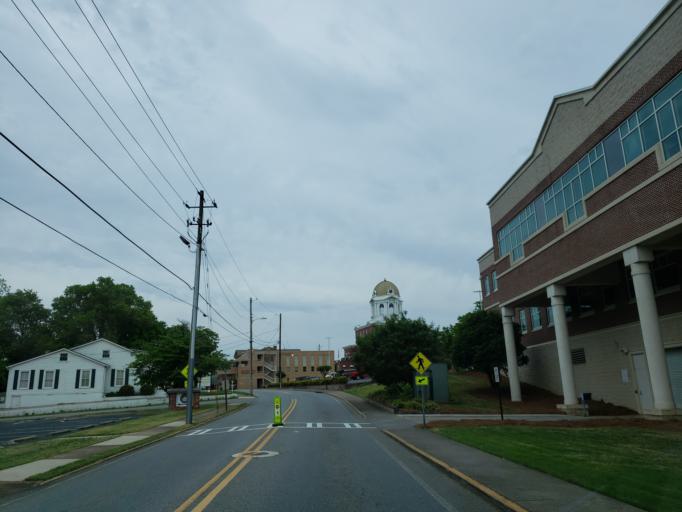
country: US
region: Georgia
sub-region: Bartow County
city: Cartersville
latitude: 34.1661
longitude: -84.7999
